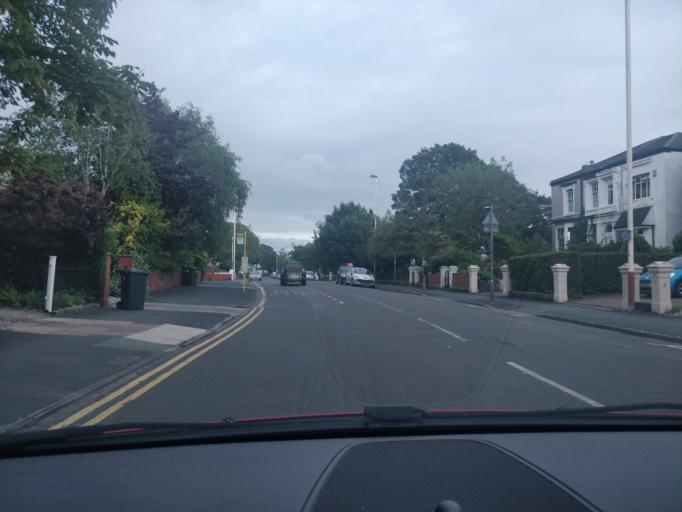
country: GB
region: England
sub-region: Sefton
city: Southport
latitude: 53.6503
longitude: -2.9958
